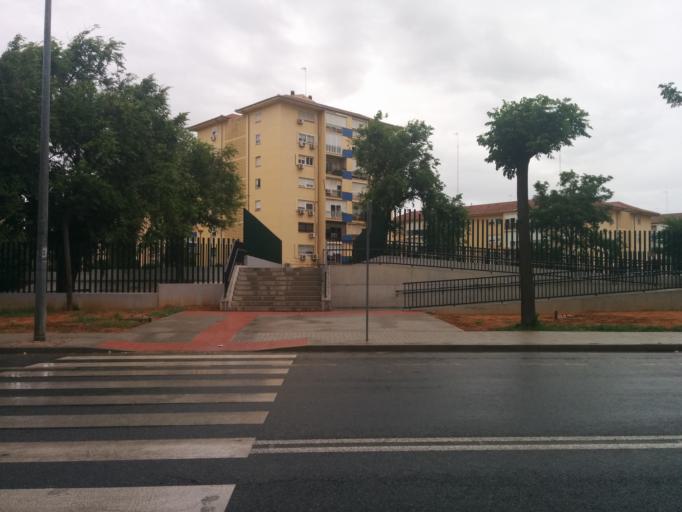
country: ES
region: Andalusia
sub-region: Provincia de Sevilla
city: Sevilla
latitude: 37.4075
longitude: -5.9181
